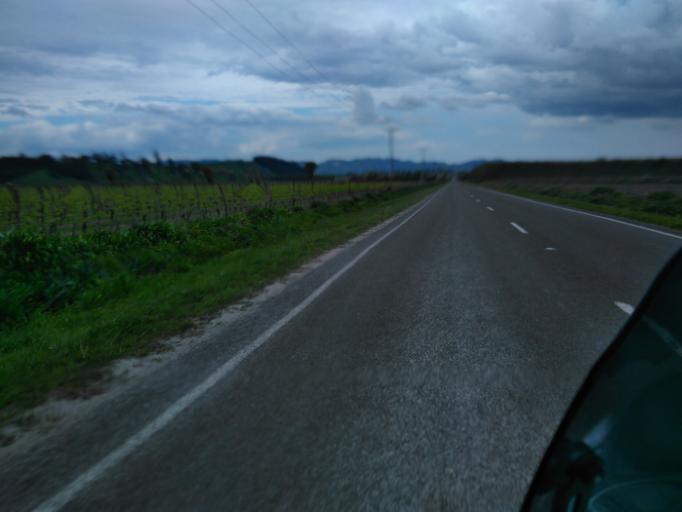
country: NZ
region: Gisborne
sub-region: Gisborne District
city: Gisborne
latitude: -38.6444
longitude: 177.8671
